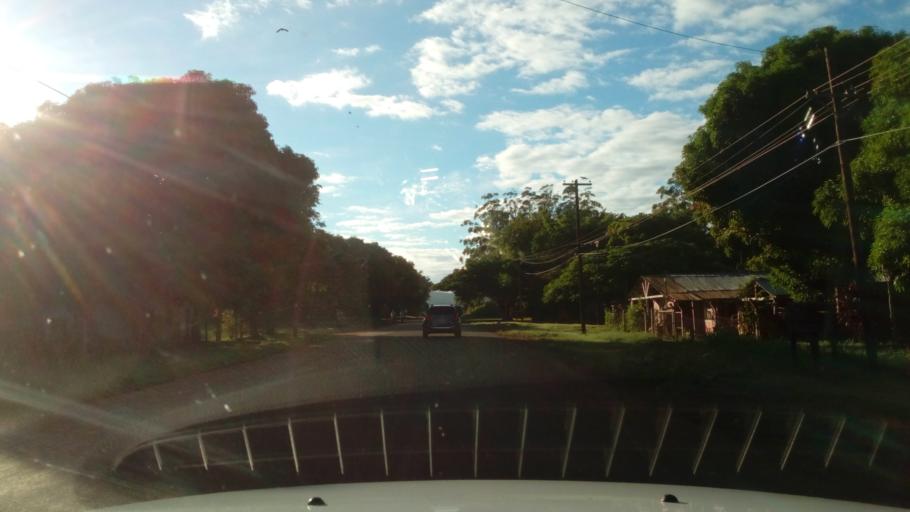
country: AR
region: Misiones
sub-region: Departamento de San Javier
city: San Javier
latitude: -27.8822
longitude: -55.1366
